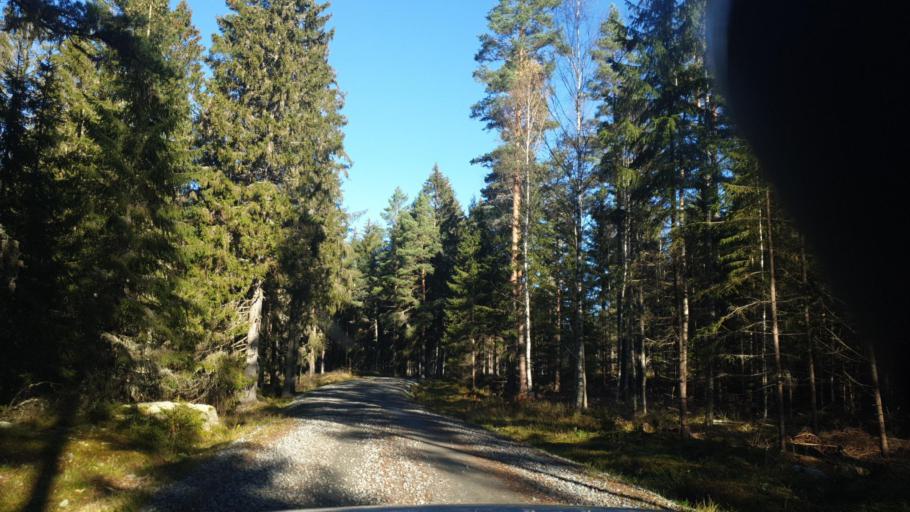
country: SE
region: Vaermland
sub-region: Karlstads Kommun
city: Valberg
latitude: 59.4547
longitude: 13.0962
